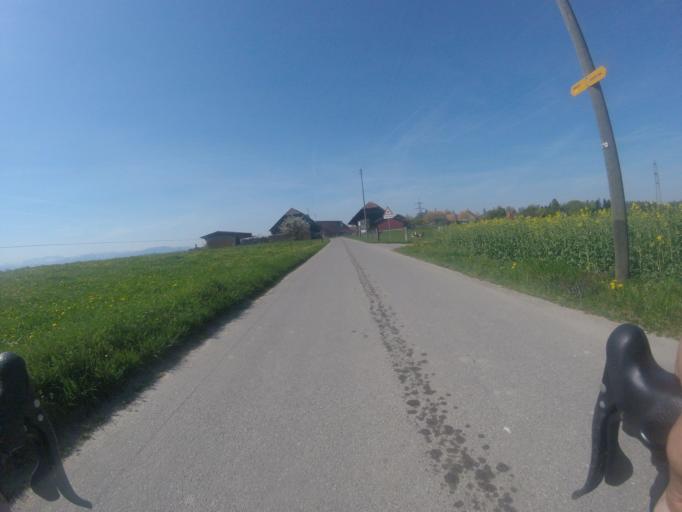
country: CH
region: Bern
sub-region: Bern-Mittelland District
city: Ferenbalm
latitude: 46.9310
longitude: 7.2269
